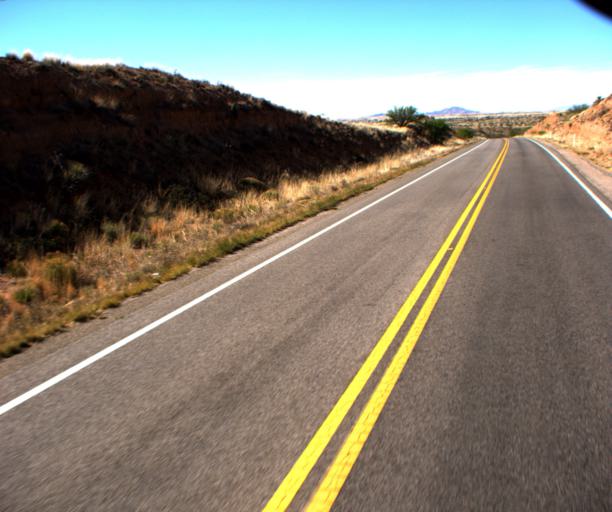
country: US
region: Arizona
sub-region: Pima County
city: Corona de Tucson
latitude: 31.7242
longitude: -110.6565
